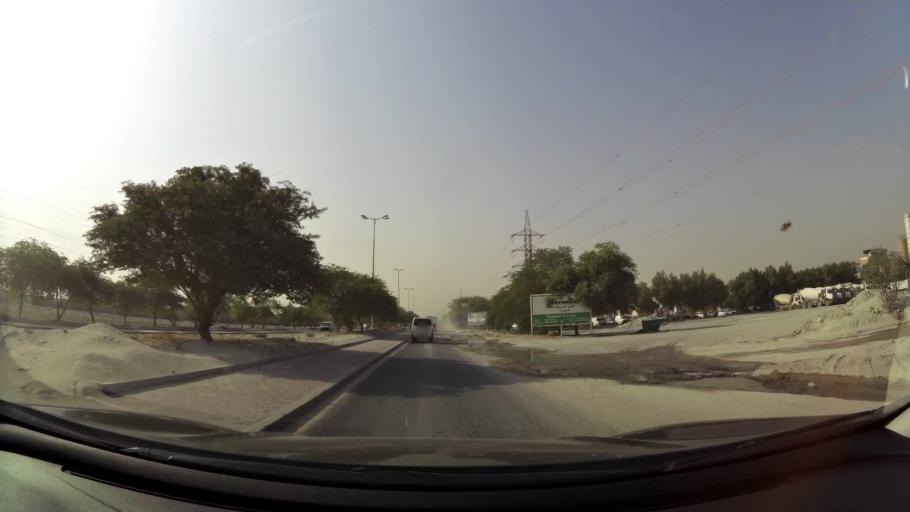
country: KW
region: Al Asimah
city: Ar Rabiyah
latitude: 29.2804
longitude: 47.8433
